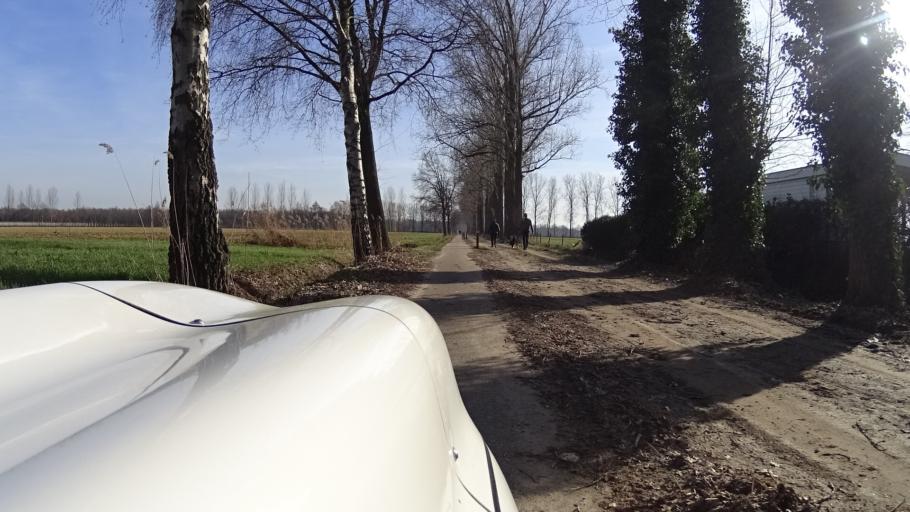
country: NL
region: North Brabant
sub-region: Gemeente Veghel
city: Mariaheide
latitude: 51.6178
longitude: 5.5698
